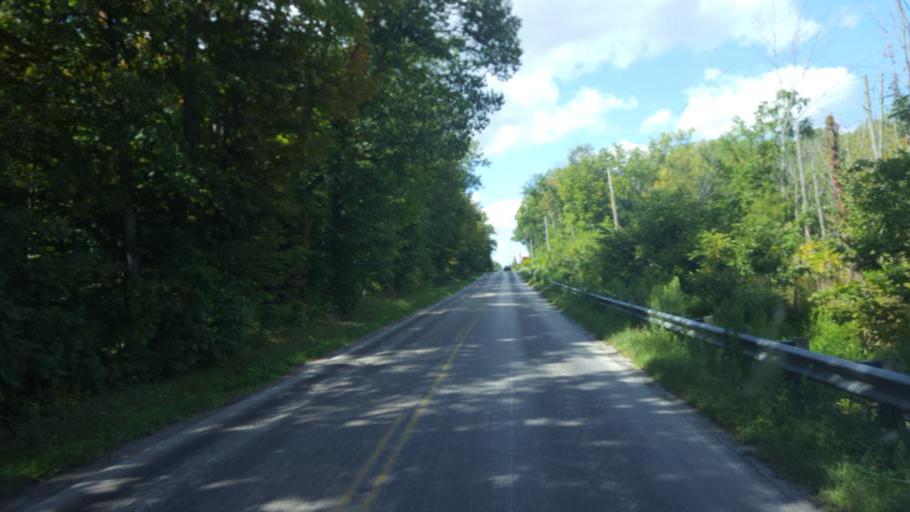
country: US
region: Ohio
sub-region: Wayne County
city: West Salem
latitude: 40.9921
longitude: -82.1695
